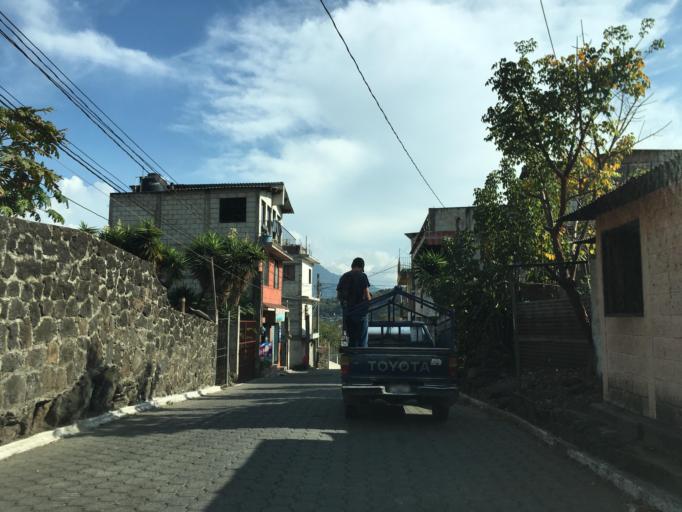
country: GT
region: Solola
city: San Antonio Palopo
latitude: 14.6660
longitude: -91.1646
